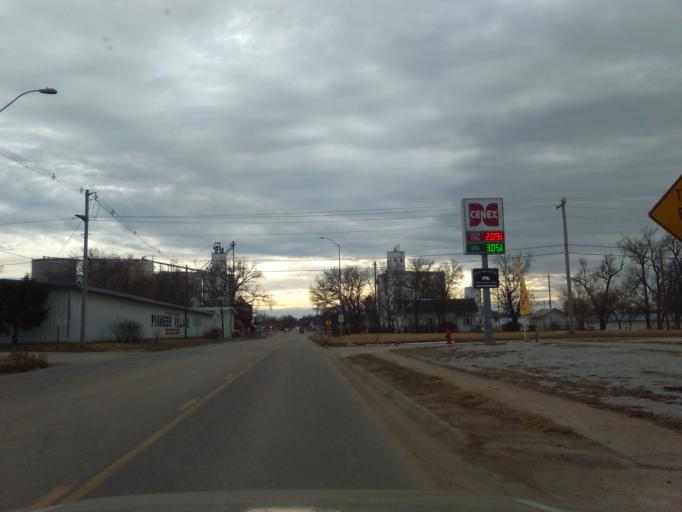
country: US
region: Nebraska
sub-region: Kearney County
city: Minden
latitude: 40.5061
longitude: -98.9519
